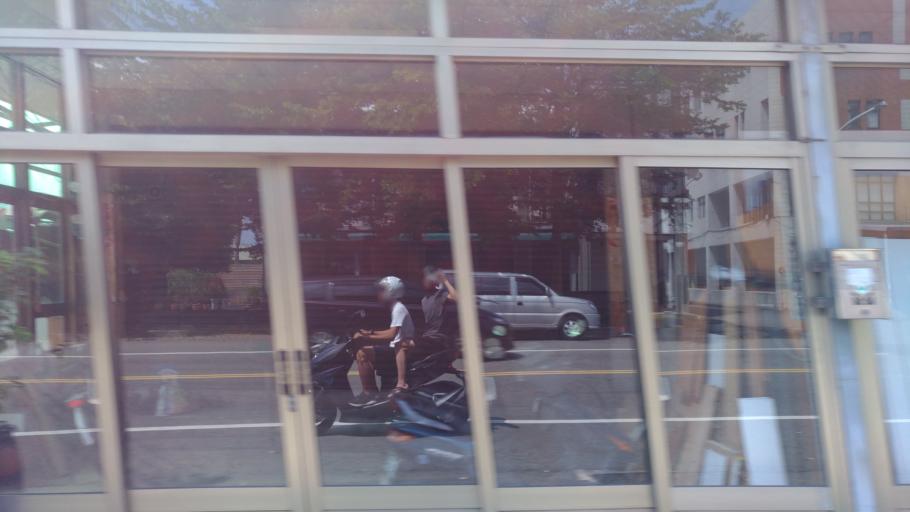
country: TW
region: Taiwan
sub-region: Yunlin
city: Douliu
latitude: 23.7566
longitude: 120.5030
